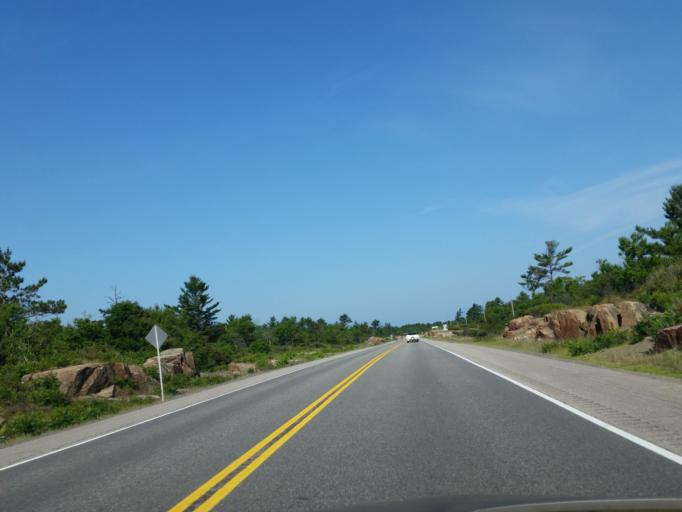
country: CA
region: Ontario
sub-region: Parry Sound District
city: Parry Sound
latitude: 45.7806
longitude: -80.5072
